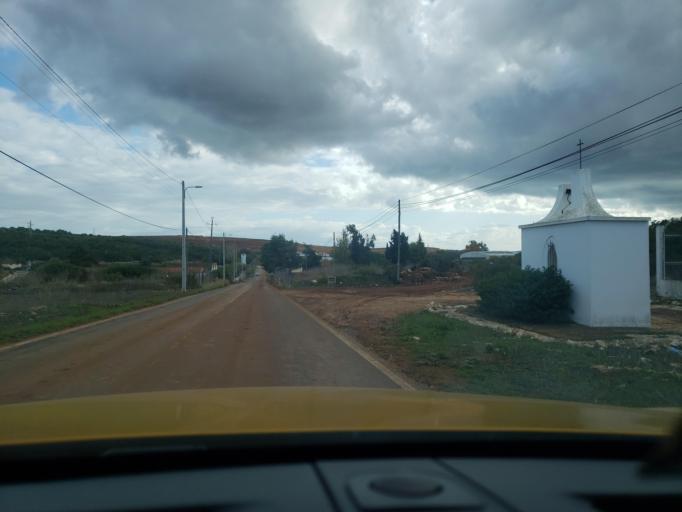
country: PT
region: Faro
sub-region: Portimao
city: Alvor
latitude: 37.1787
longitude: -8.5815
